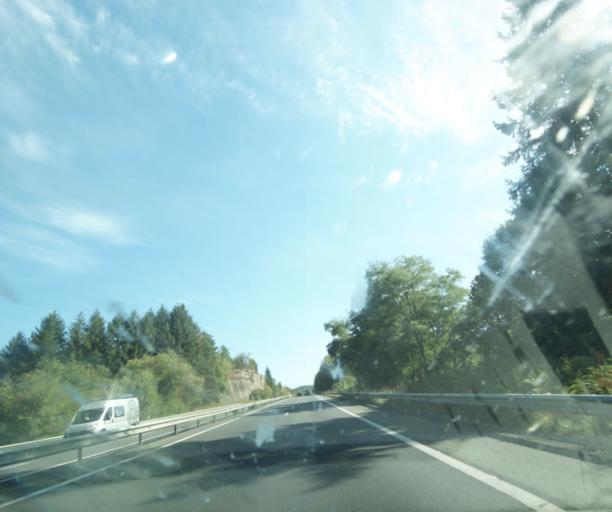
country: FR
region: Limousin
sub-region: Departement de la Correze
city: Brive-la-Gaillarde
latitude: 45.1251
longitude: 1.4954
